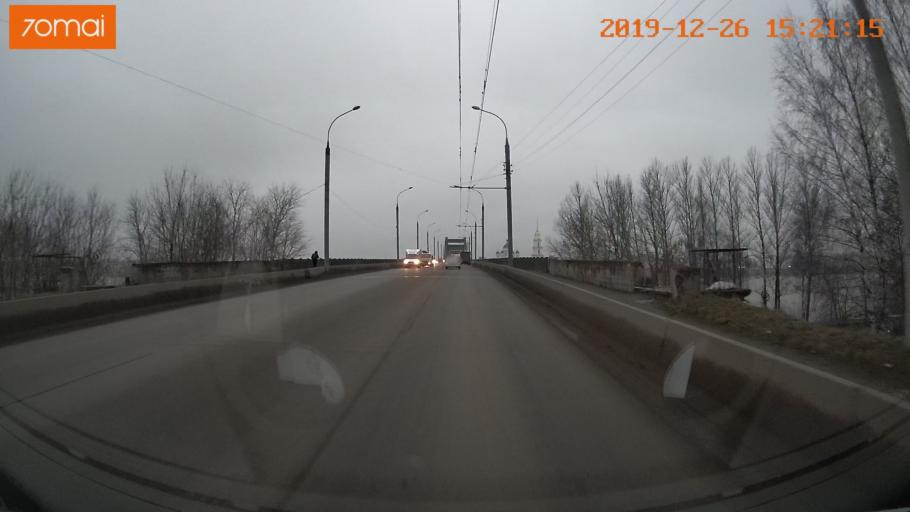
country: RU
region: Jaroslavl
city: Rybinsk
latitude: 58.0546
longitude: 38.8642
